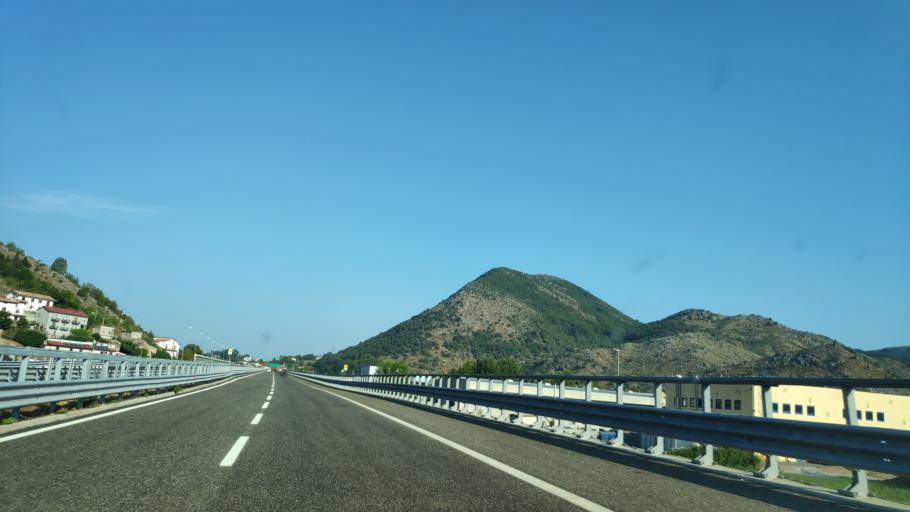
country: IT
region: Basilicate
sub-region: Provincia di Potenza
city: Lauria
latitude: 40.0136
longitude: 15.8980
